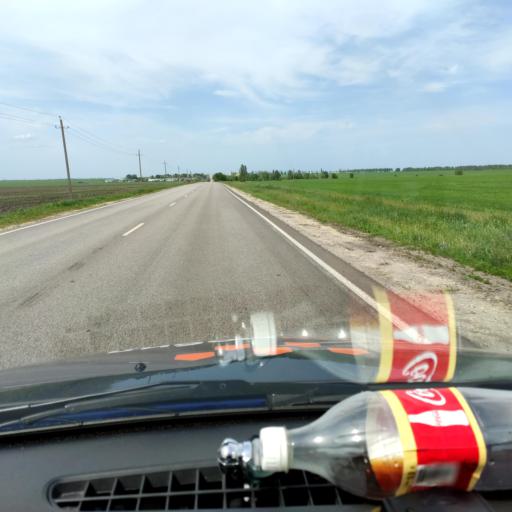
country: RU
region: Voronezj
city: Novaya Usman'
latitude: 51.5655
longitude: 39.3758
